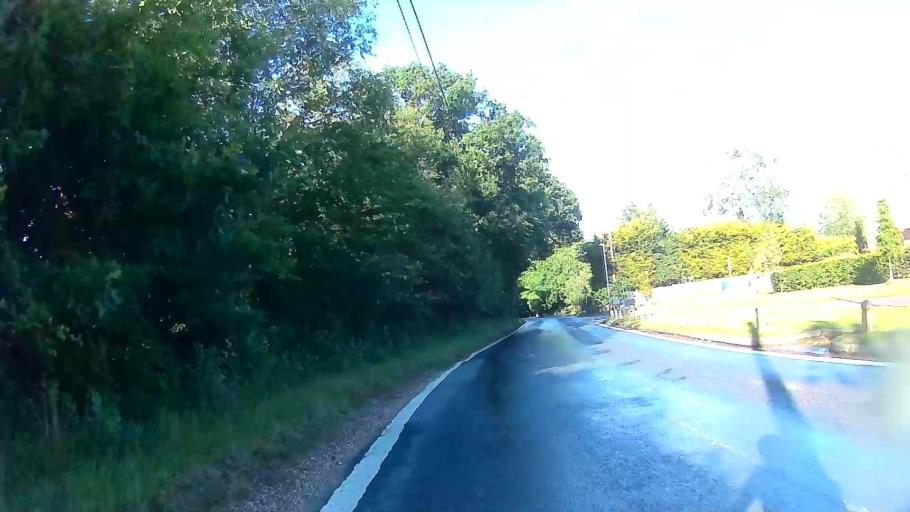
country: GB
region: England
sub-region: Essex
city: Writtle
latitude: 51.7147
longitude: 0.3896
